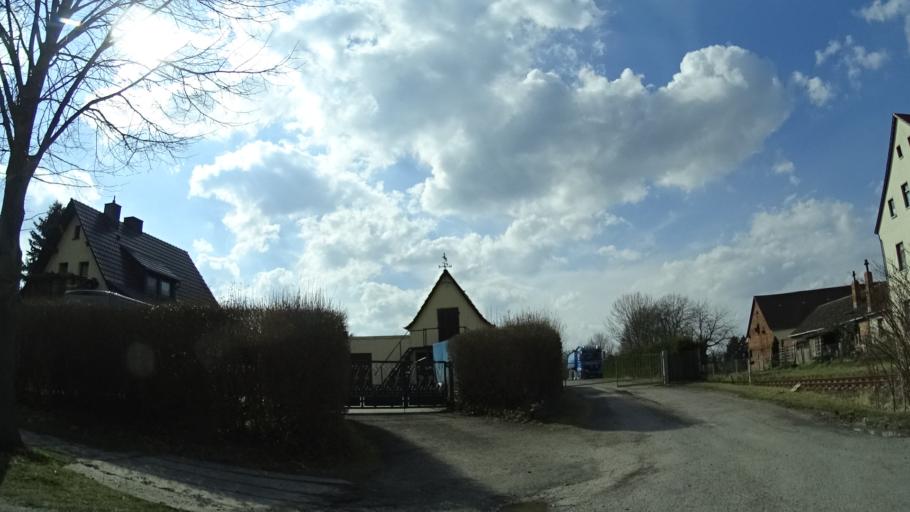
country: DE
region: Saxony-Anhalt
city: Stossen
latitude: 51.1115
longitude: 11.9273
